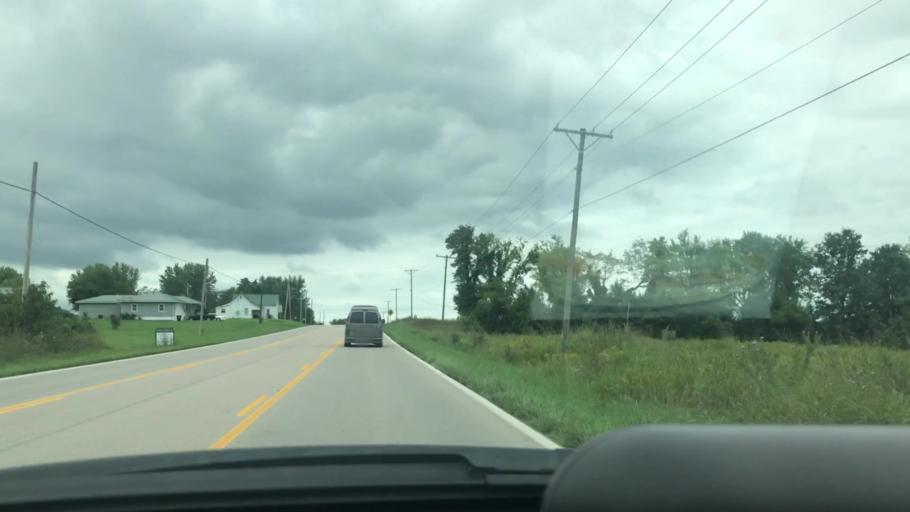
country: US
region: Missouri
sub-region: Dallas County
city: Buffalo
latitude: 37.6501
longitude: -93.1039
